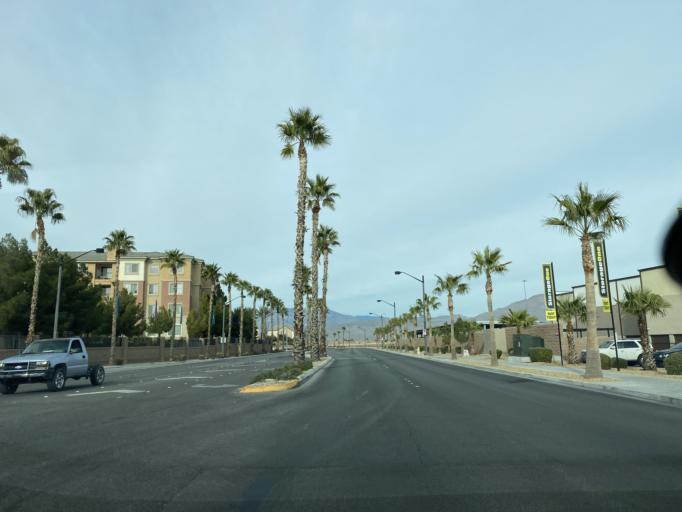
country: US
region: Nevada
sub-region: Clark County
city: Summerlin South
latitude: 36.2976
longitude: -115.2895
